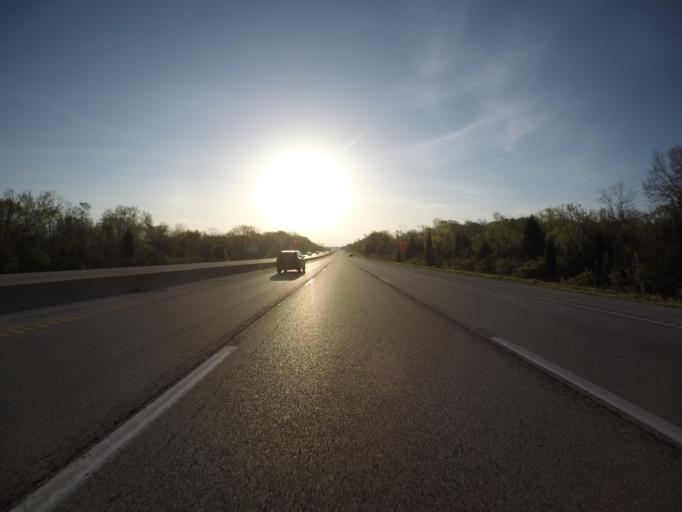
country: US
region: Missouri
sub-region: Jackson County
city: Grandview
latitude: 38.9384
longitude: -94.5023
